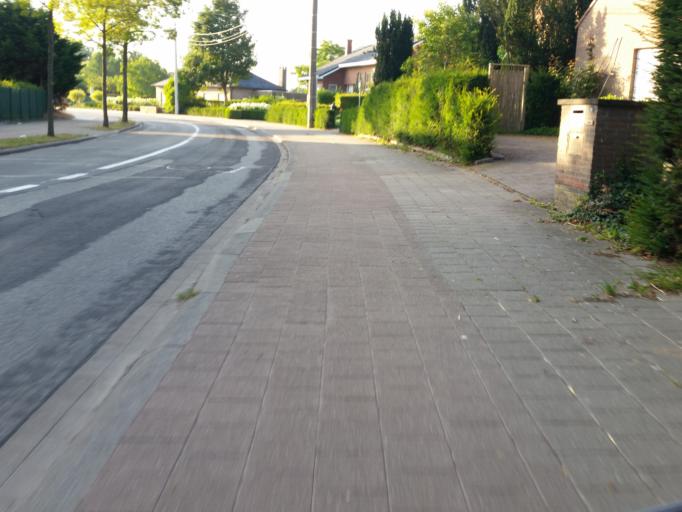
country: BE
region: Flanders
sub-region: Provincie Vlaams-Brabant
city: Zemst
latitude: 50.9751
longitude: 4.4292
